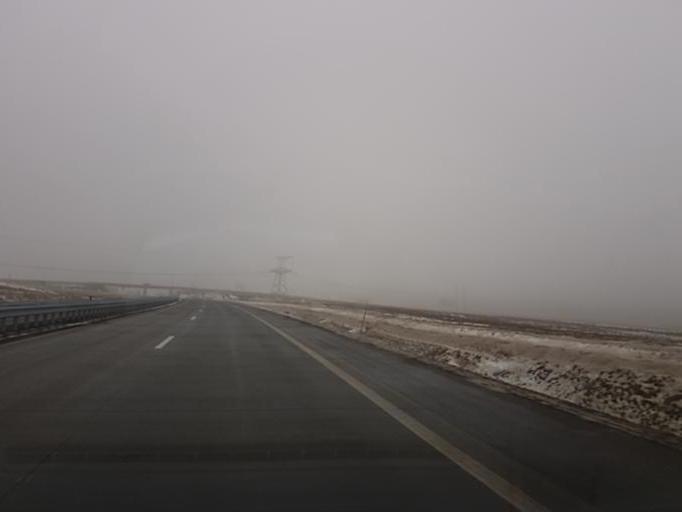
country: BY
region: Minsk
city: Atolina
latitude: 53.7611
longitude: 27.3991
